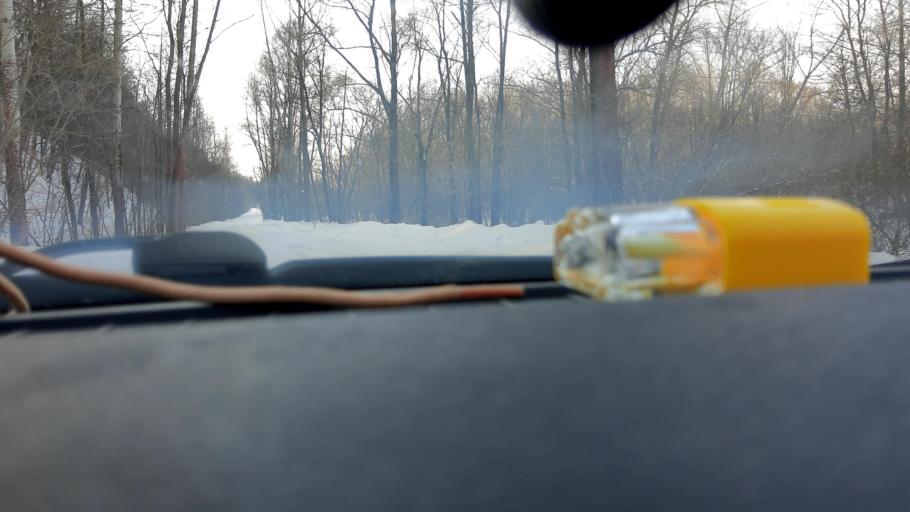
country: RU
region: Bashkortostan
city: Kabakovo
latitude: 54.6270
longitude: 56.0507
